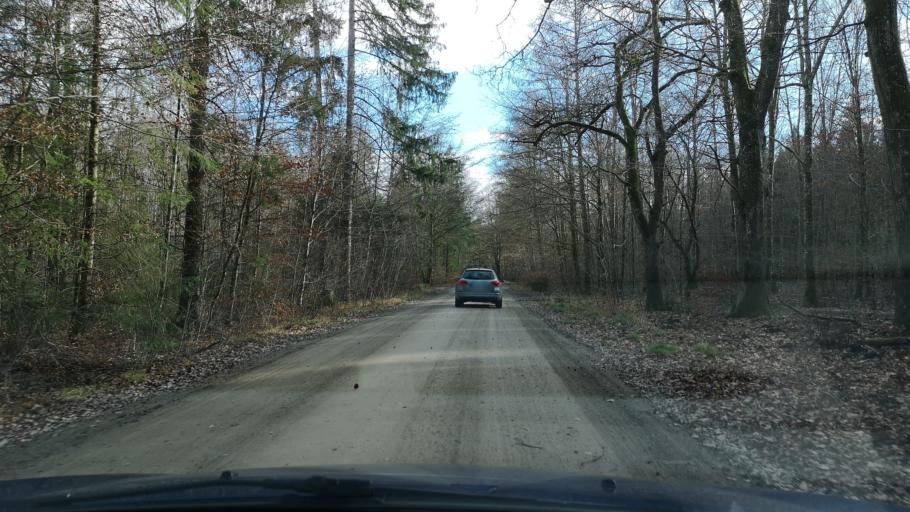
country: DE
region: Bavaria
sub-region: Upper Bavaria
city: Ebersberg
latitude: 48.1034
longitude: 11.9366
